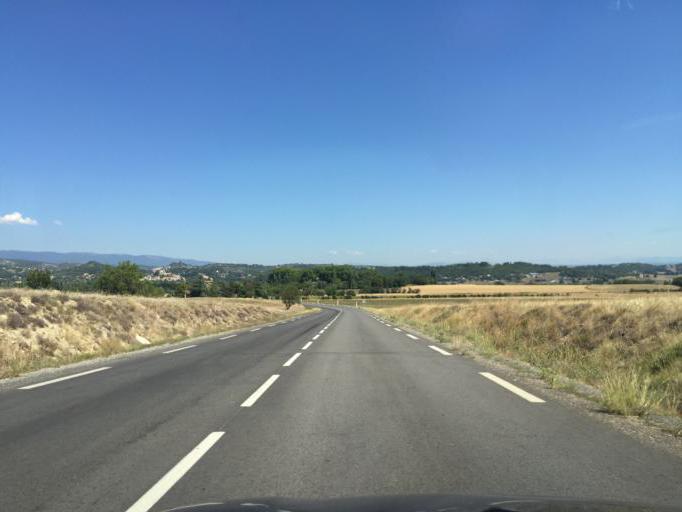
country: FR
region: Provence-Alpes-Cote d'Azur
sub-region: Departement des Alpes-de-Haute-Provence
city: Mane
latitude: 43.9144
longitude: 5.7535
